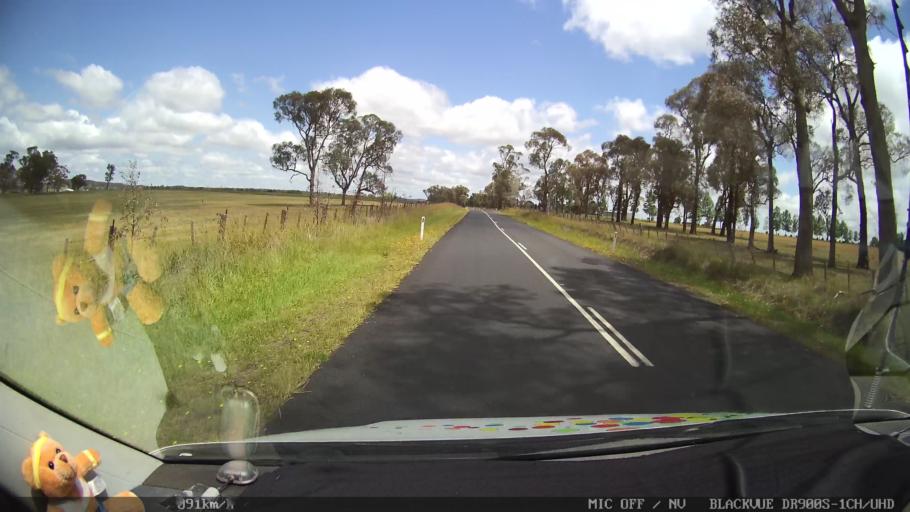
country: AU
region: New South Wales
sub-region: Glen Innes Severn
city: Glen Innes
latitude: -29.6487
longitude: 151.6926
